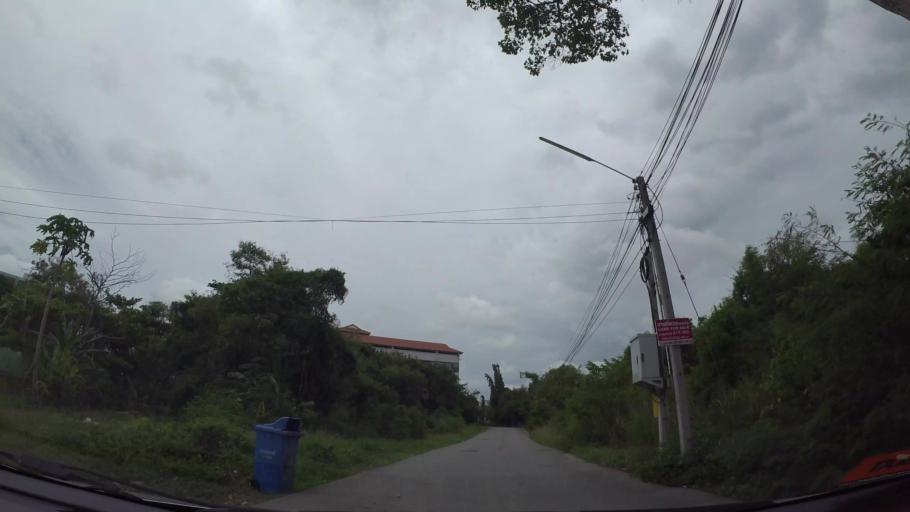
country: TH
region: Chon Buri
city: Sattahip
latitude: 12.7592
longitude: 100.8817
